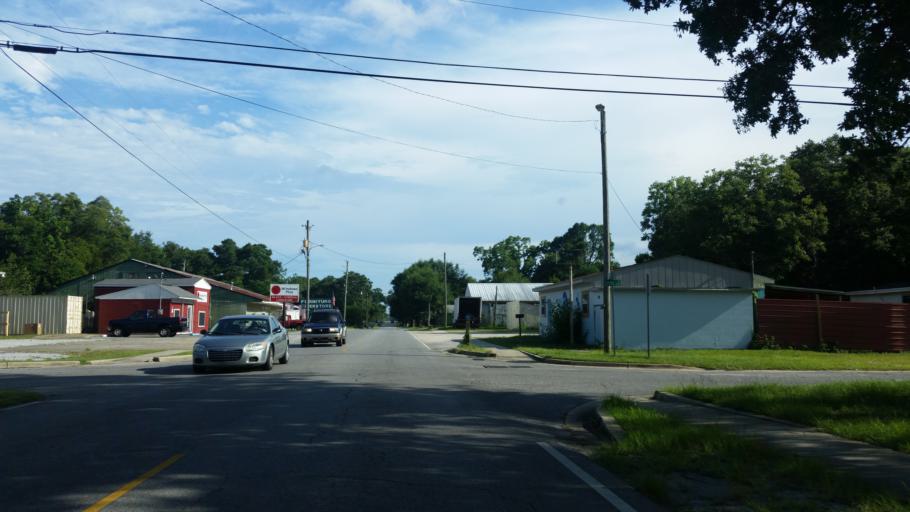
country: US
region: Florida
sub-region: Escambia County
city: Goulding
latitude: 30.4404
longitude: -87.2457
